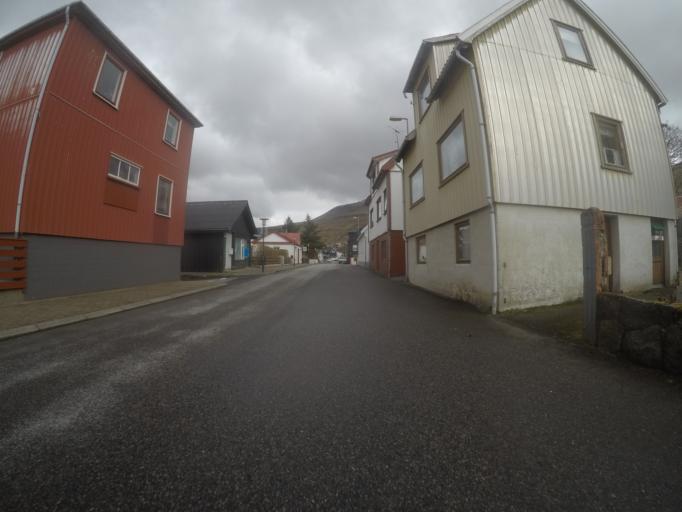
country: FO
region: Vagar
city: Midvagur
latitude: 62.0536
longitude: -7.1498
